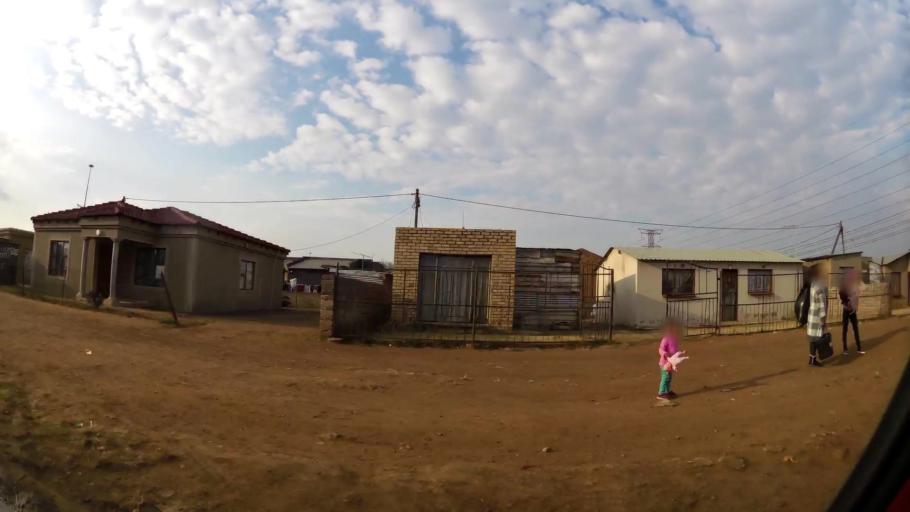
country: ZA
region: Gauteng
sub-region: Sedibeng District Municipality
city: Vanderbijlpark
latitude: -26.6798
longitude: 27.8700
